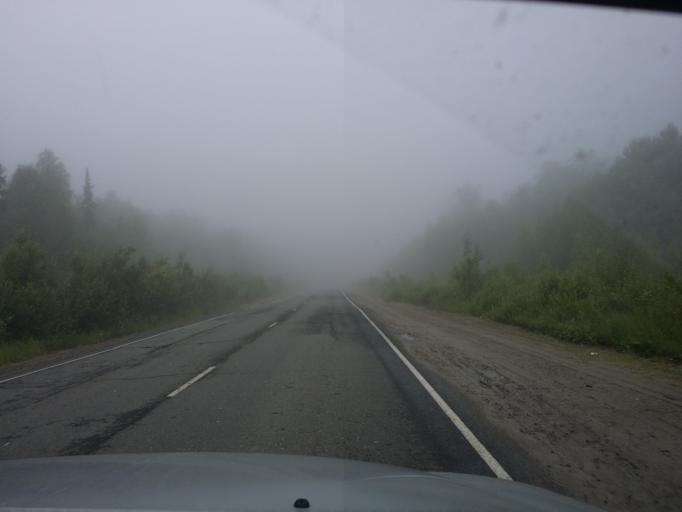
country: RU
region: Khanty-Mansiyskiy Avtonomnyy Okrug
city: Gornopravdinsk
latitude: 59.6385
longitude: 69.8437
